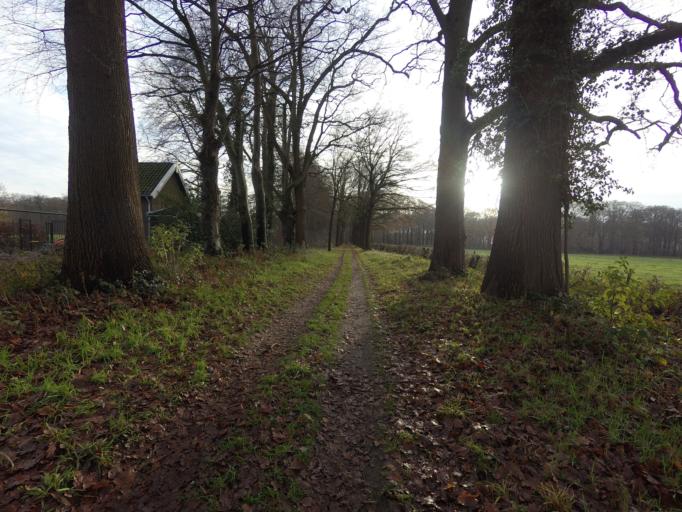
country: NL
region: North Holland
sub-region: Gemeente Wijdemeren
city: Kortenhoef
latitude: 52.2372
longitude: 5.1303
